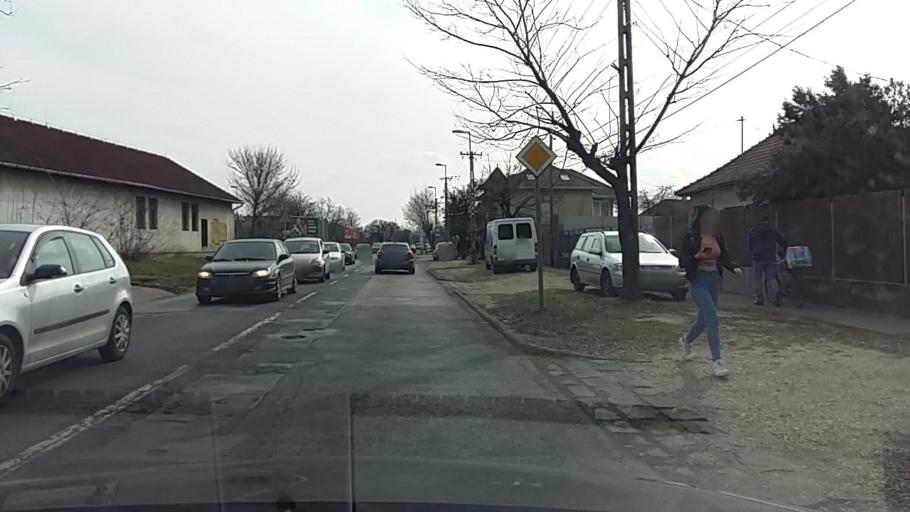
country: HU
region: Budapest
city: Budapest XVIII. keruelet
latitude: 47.4136
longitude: 19.1730
